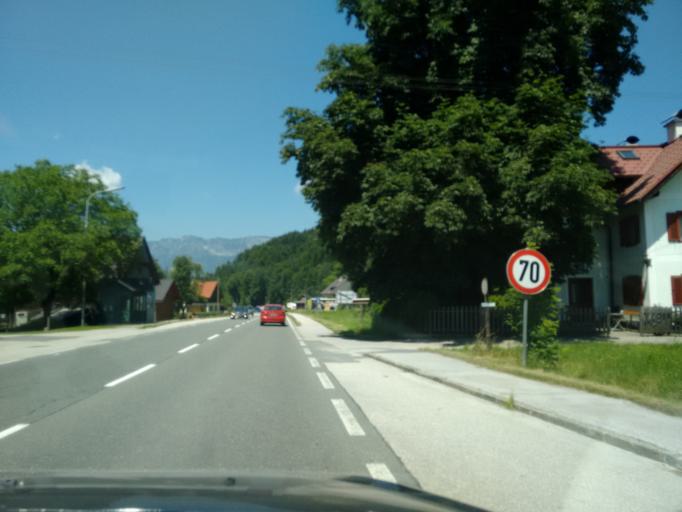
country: AT
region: Upper Austria
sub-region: Politischer Bezirk Gmunden
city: Bad Goisern
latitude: 47.6244
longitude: 13.6446
